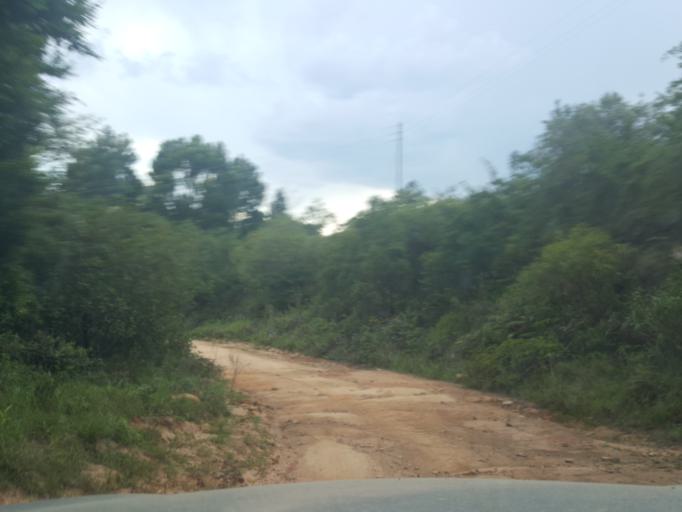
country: ZA
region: Limpopo
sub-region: Mopani District Municipality
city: Hoedspruit
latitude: -24.5819
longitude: 30.8627
